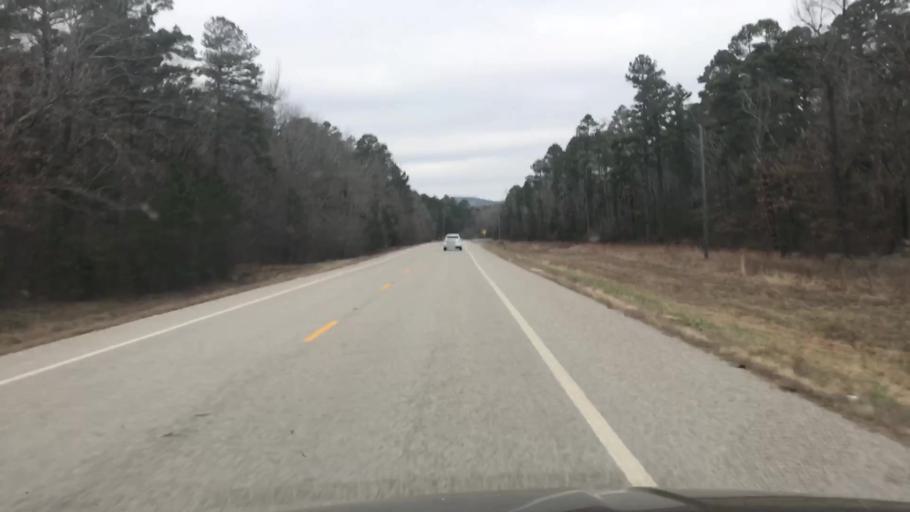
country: US
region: Arkansas
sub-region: Scott County
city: Waldron
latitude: 34.7136
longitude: -93.9435
